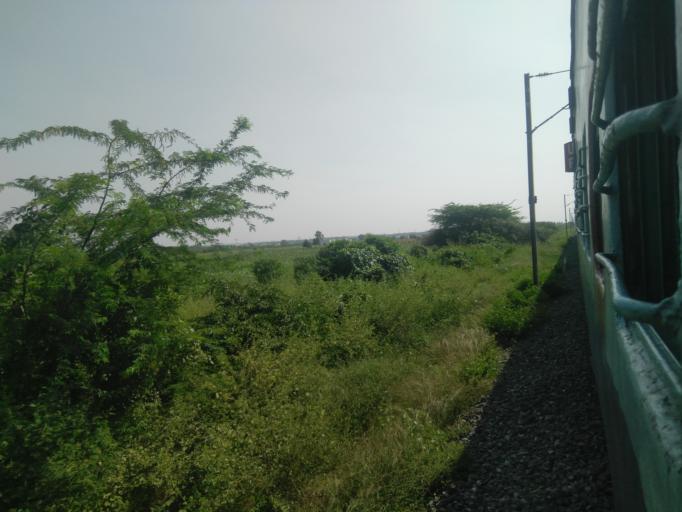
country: IN
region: Tamil Nadu
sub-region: Coimbatore
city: Periyanayakkanpalaiyam
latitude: 11.1298
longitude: 76.9486
